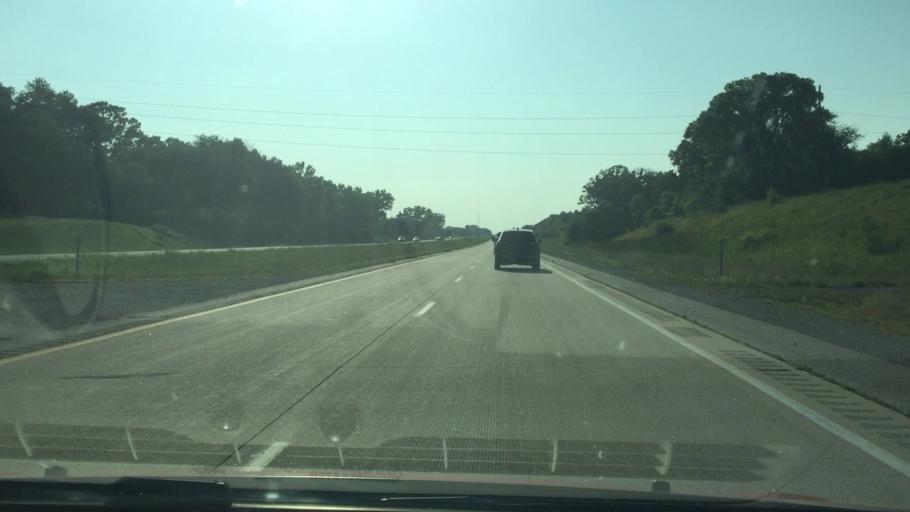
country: US
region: Iowa
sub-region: Scott County
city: Blue Grass
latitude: 41.5153
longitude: -90.8223
